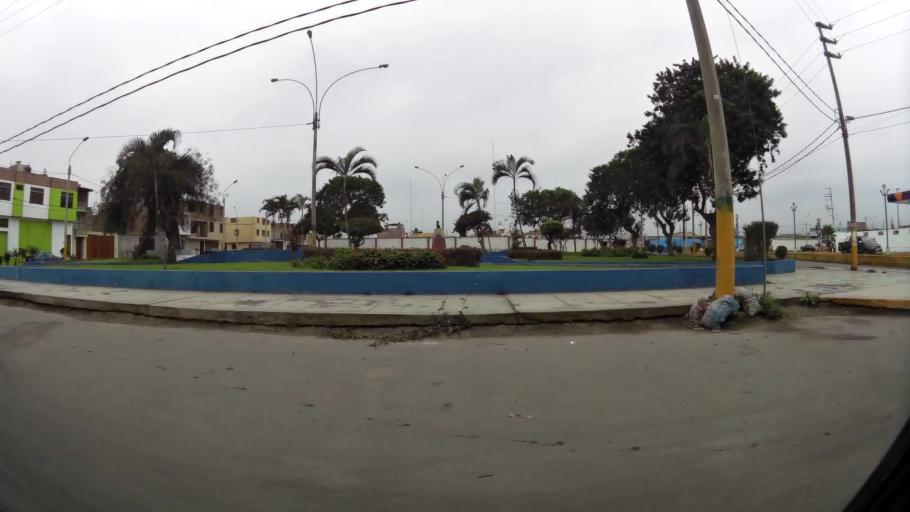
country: PE
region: Lima
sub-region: Barranca
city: Barranca
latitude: -10.7442
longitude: -77.7658
